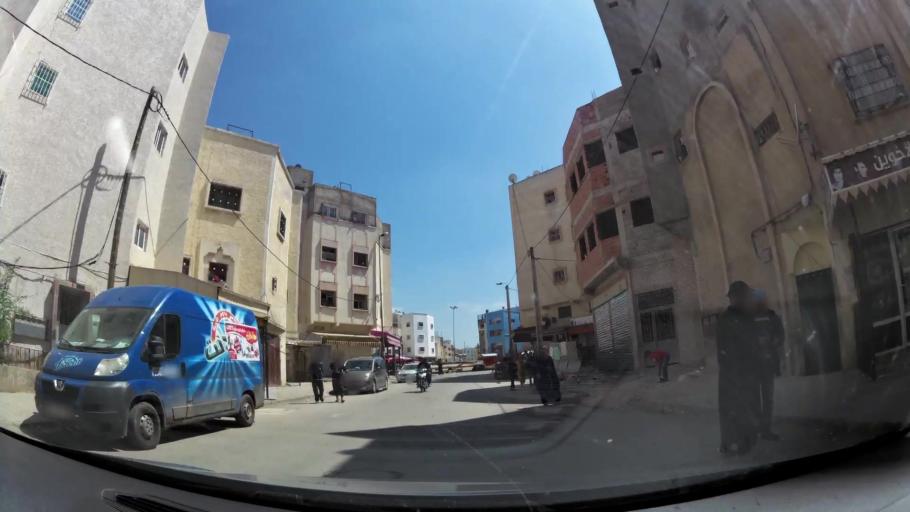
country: MA
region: Fes-Boulemane
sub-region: Fes
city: Fes
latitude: 34.0129
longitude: -5.0280
